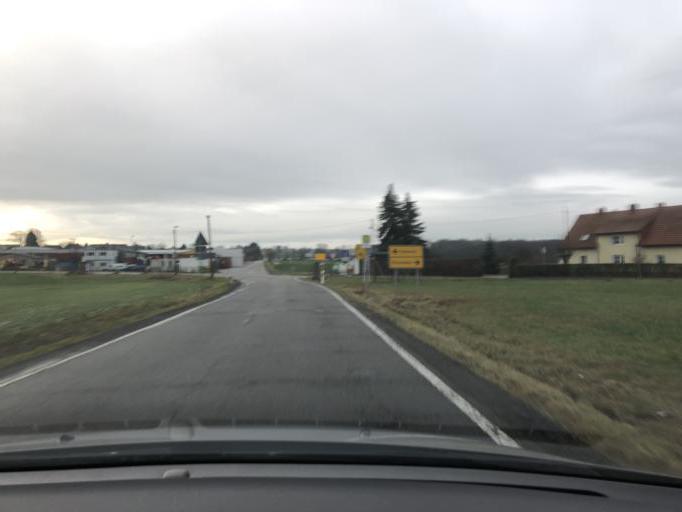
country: DE
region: Saxony
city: Limbach-Oberfrohna
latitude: 50.8670
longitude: 12.7295
